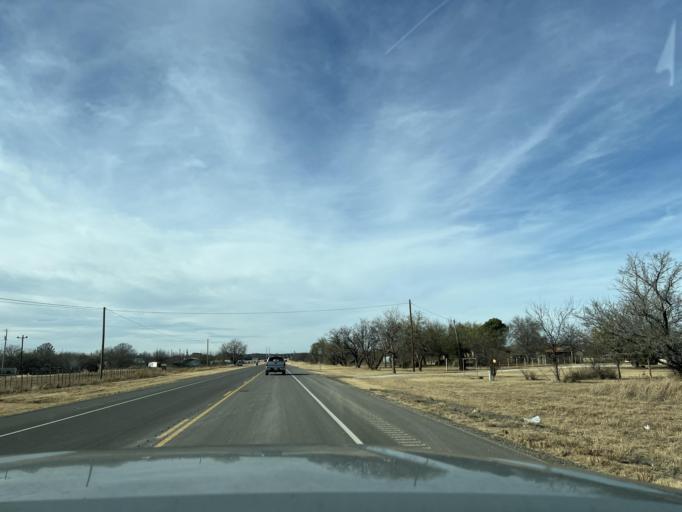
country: US
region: Texas
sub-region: Shackelford County
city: Albany
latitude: 32.7164
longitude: -99.2846
